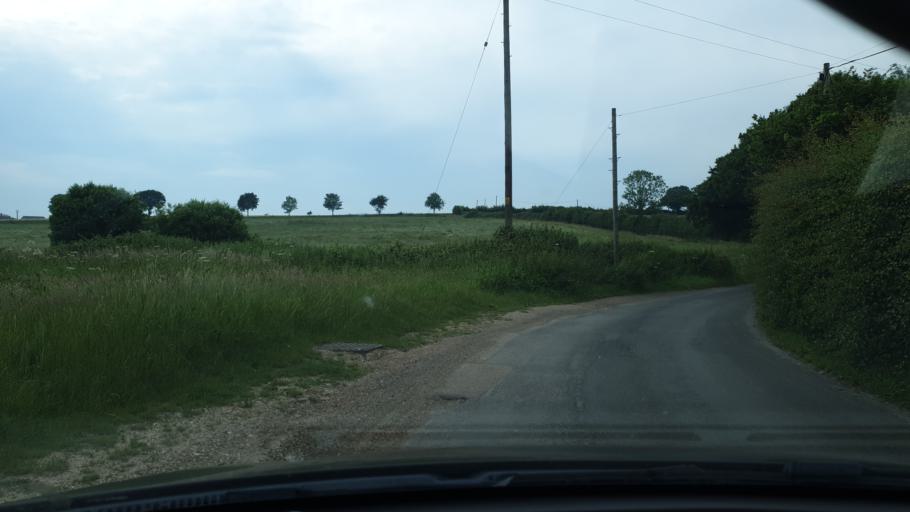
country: GB
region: England
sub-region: Essex
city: Dovercourt
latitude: 51.9153
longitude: 1.2069
